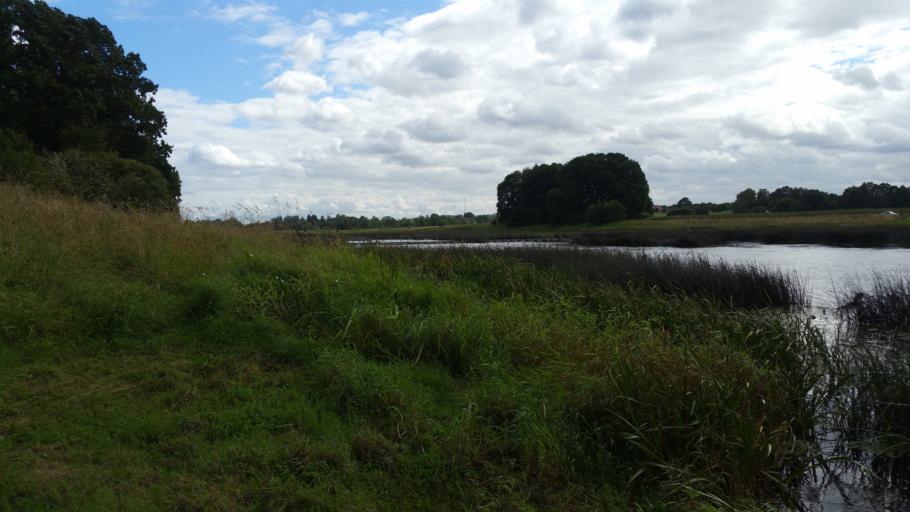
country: LV
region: Rundales
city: Pilsrundale
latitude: 56.4390
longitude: 24.0505
